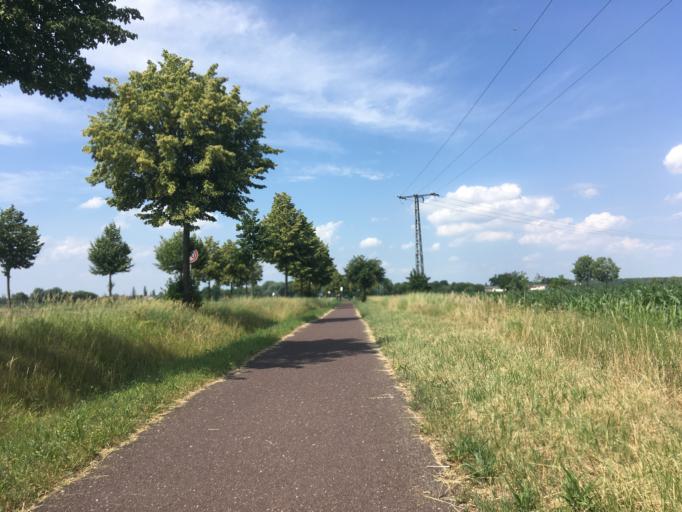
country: DE
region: Saxony-Anhalt
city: Osternienburg
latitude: 51.7528
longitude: 12.0233
